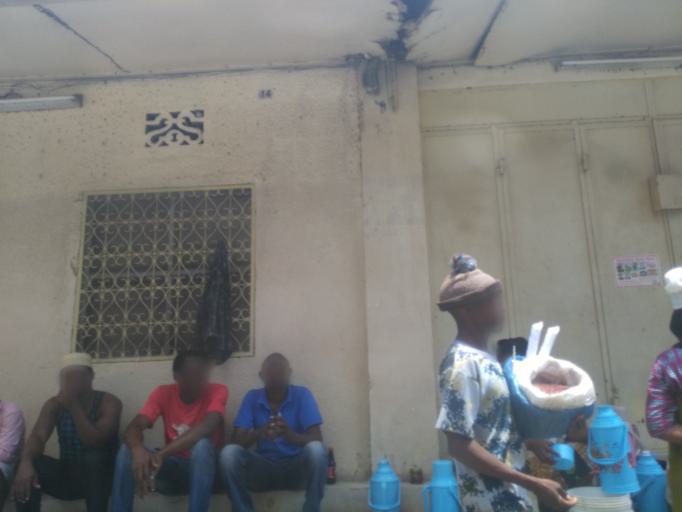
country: TZ
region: Dar es Salaam
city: Dar es Salaam
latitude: -6.8244
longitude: 39.2759
